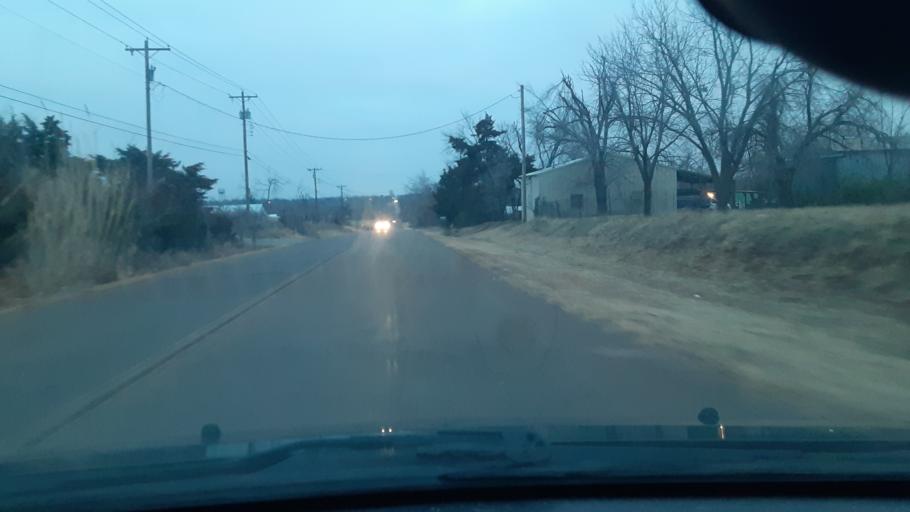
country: US
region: Oklahoma
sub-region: Logan County
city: Guthrie
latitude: 35.8631
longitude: -97.4076
